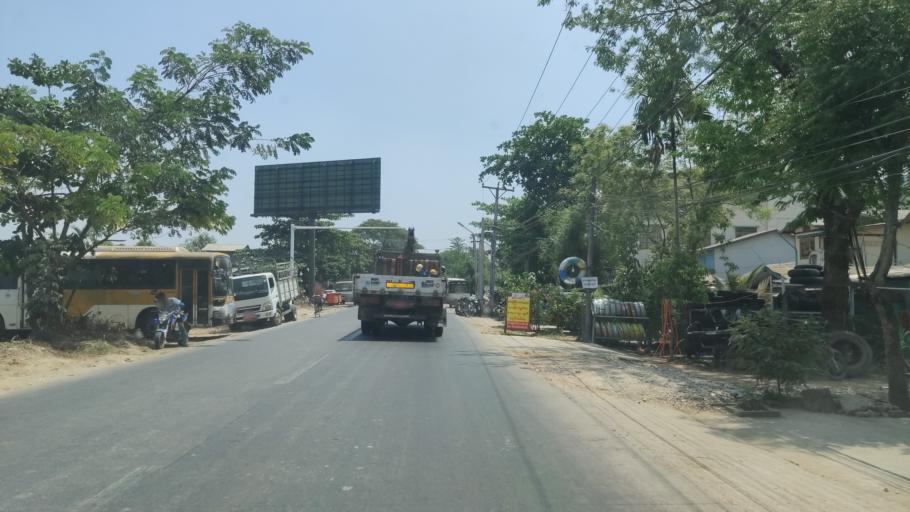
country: MM
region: Yangon
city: Yangon
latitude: 16.8942
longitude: 96.2178
